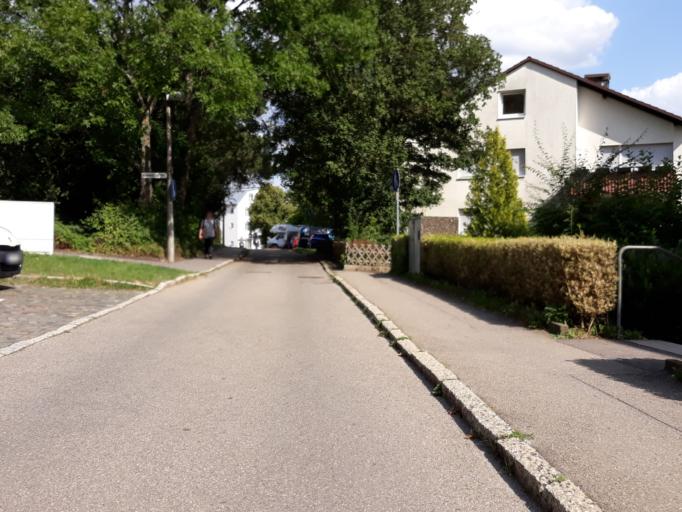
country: DE
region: Baden-Wuerttemberg
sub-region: Regierungsbezirk Stuttgart
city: Sindelfingen
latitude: 48.6980
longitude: 9.0168
